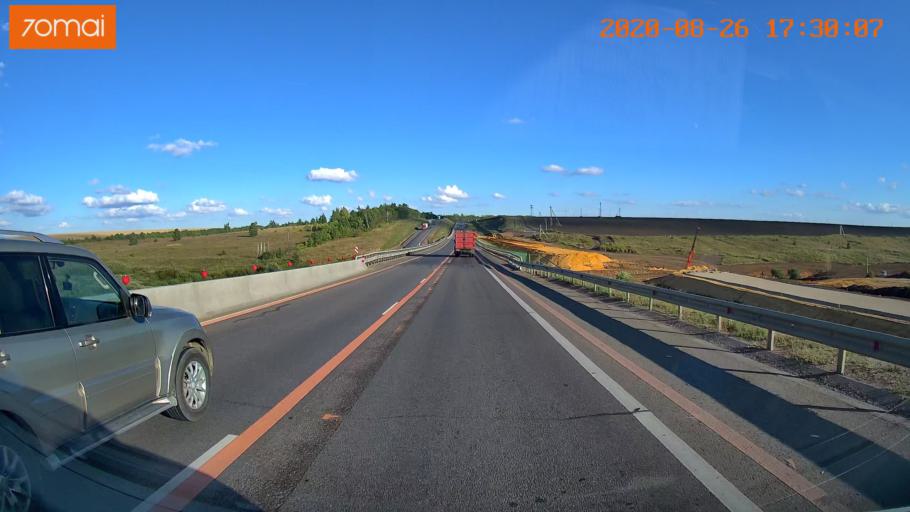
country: RU
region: Tula
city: Kazachka
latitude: 53.4479
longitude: 38.1633
